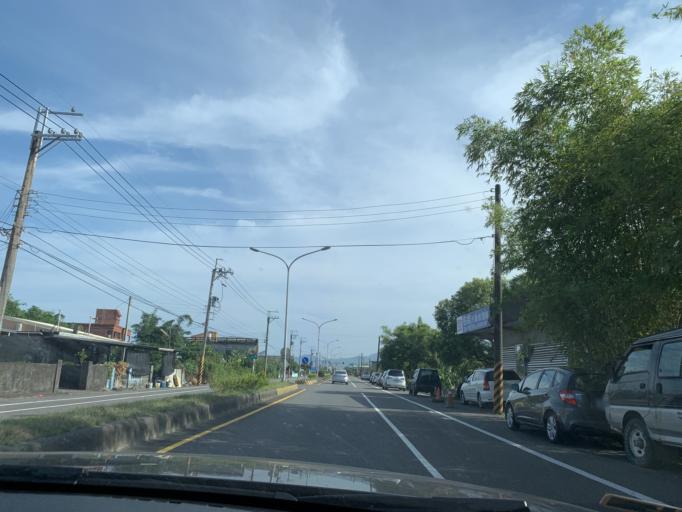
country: TW
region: Taiwan
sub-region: Yilan
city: Yilan
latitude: 24.7459
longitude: 121.8163
